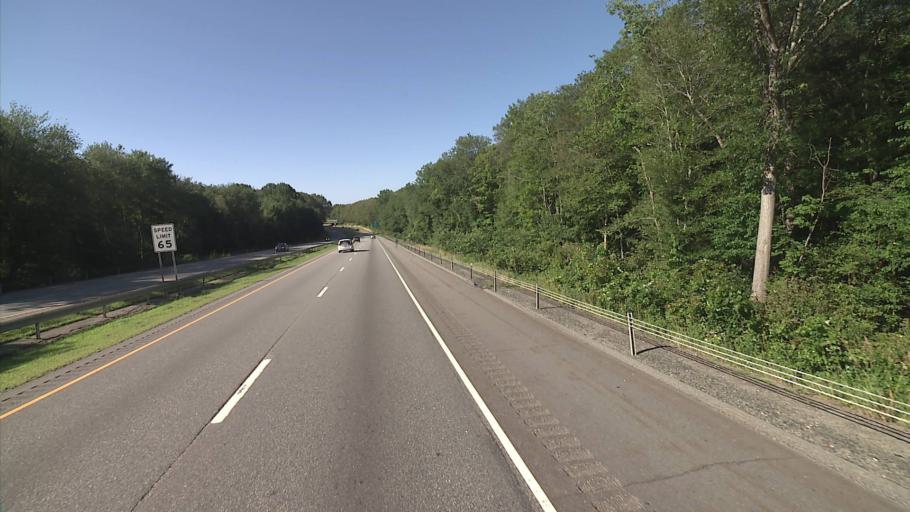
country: US
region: Connecticut
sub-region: New London County
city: Norwich
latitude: 41.5232
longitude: -72.1184
